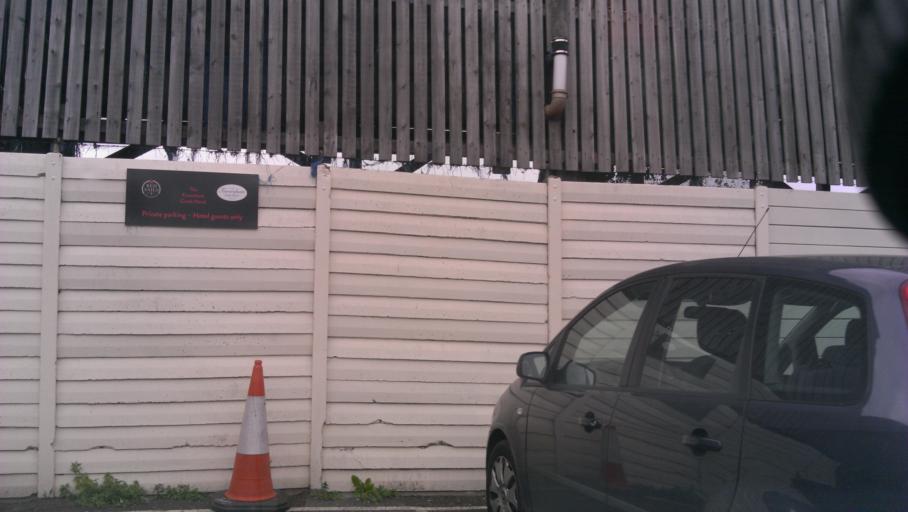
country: GB
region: England
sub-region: Kent
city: Faversham
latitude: 51.3180
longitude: 0.8919
